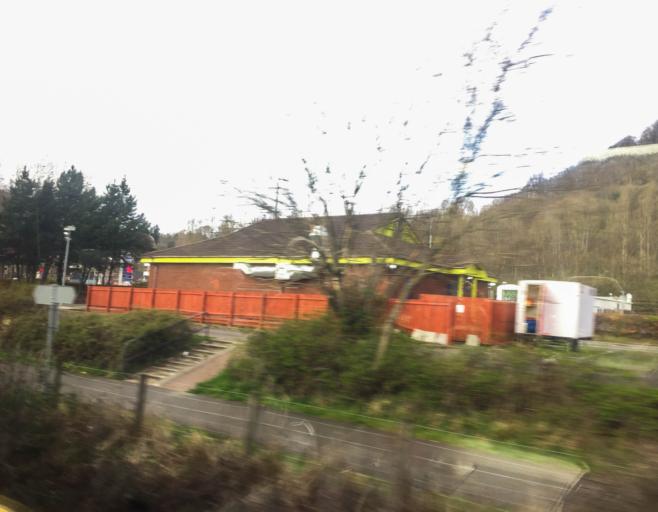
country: GB
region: Scotland
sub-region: Renfrewshire
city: Bishopton
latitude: 55.9349
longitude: -4.5152
